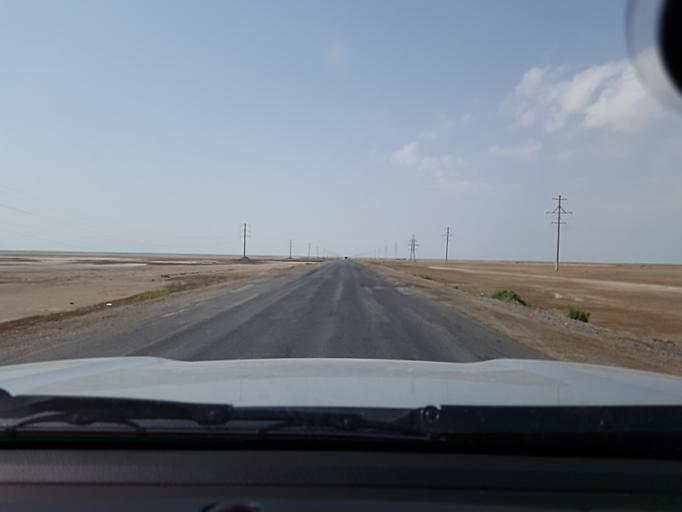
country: TM
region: Balkan
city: Gumdag
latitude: 39.0855
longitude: 54.5844
